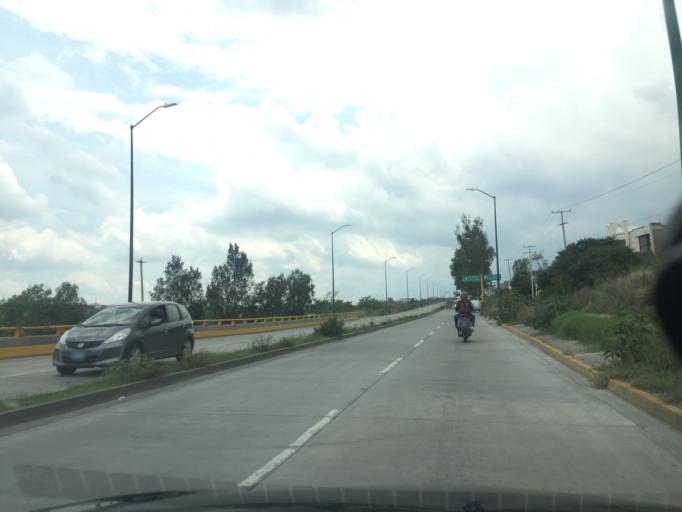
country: MX
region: Guanajuato
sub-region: Leon
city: La Ermita
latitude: 21.1464
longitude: -101.7162
